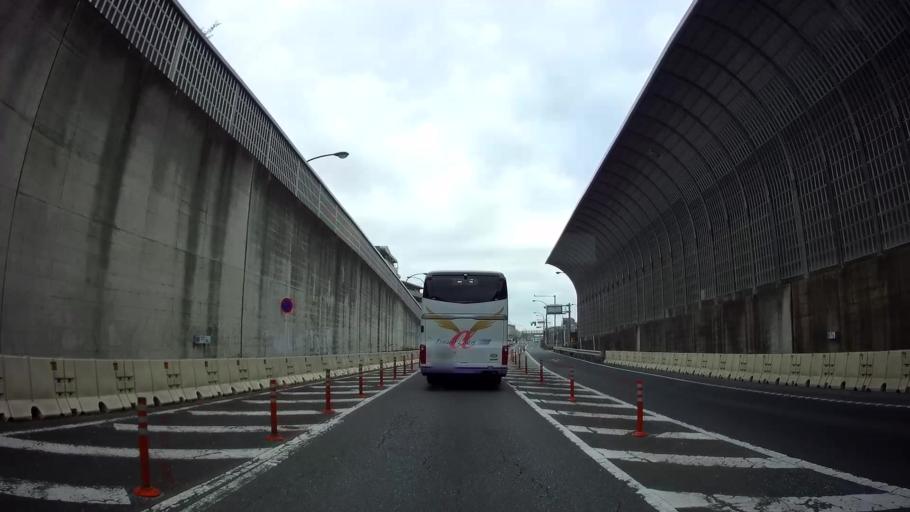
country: JP
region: Saitama
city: Wako
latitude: 35.7720
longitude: 139.6513
